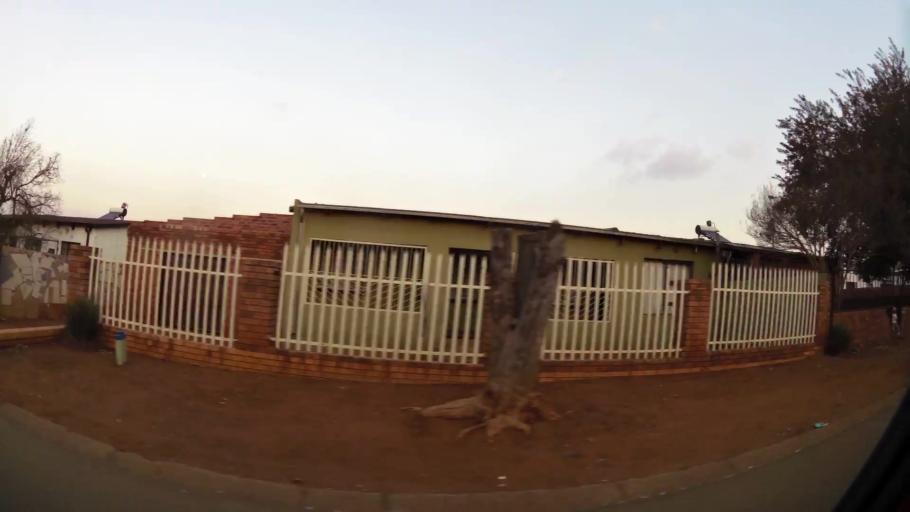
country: ZA
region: Gauteng
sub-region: City of Johannesburg Metropolitan Municipality
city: Soweto
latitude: -26.2850
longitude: 27.8782
